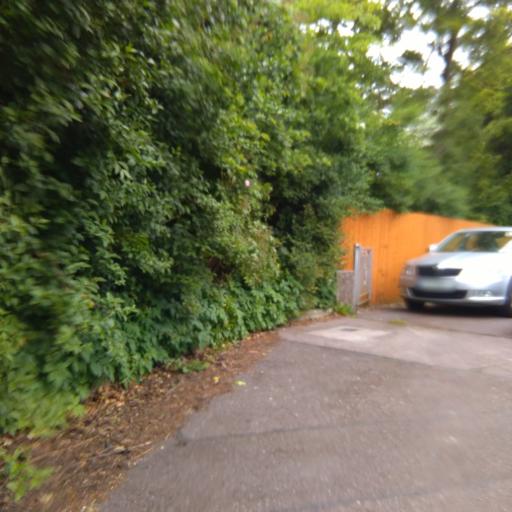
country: IE
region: Munster
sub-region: County Cork
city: Cork
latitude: 51.9140
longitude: -8.4471
